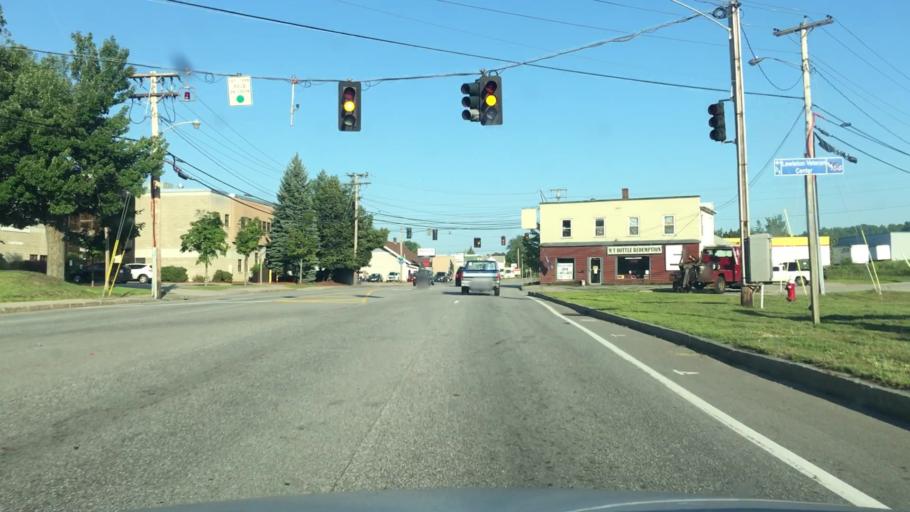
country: US
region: Maine
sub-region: Androscoggin County
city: Lewiston
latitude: 44.0739
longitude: -70.1783
